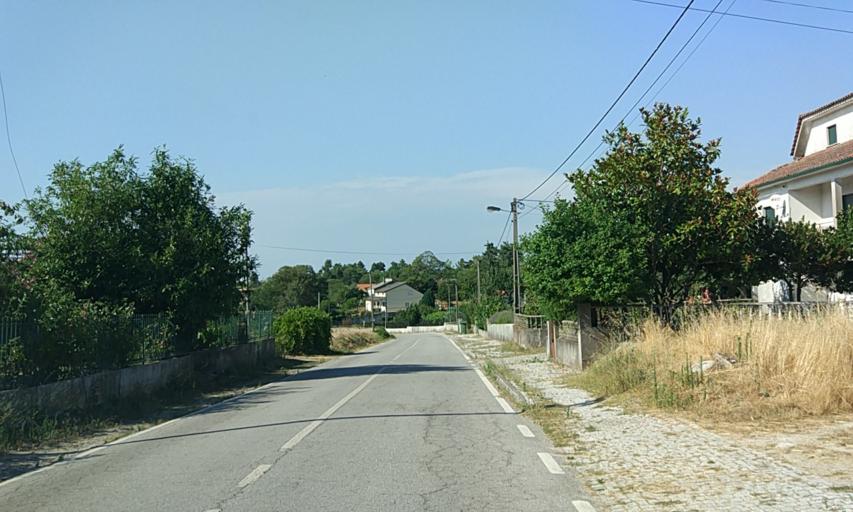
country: PT
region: Vila Real
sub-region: Murca
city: Murca
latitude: 41.3208
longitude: -7.4618
